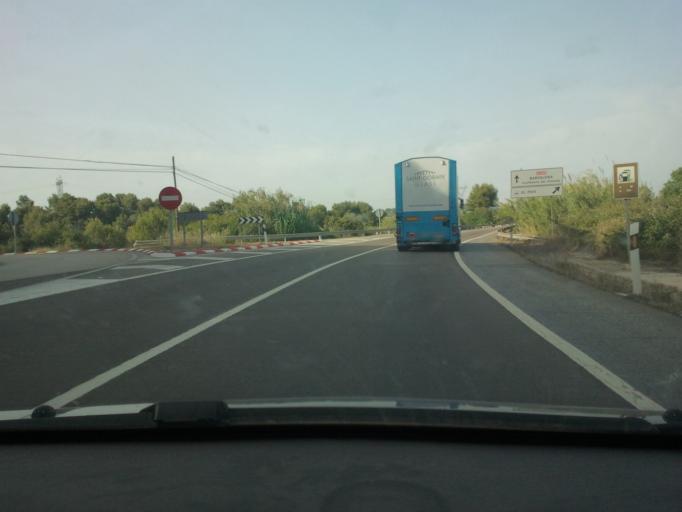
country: ES
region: Catalonia
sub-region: Provincia de Barcelona
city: Castellet
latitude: 41.2828
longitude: 1.6144
